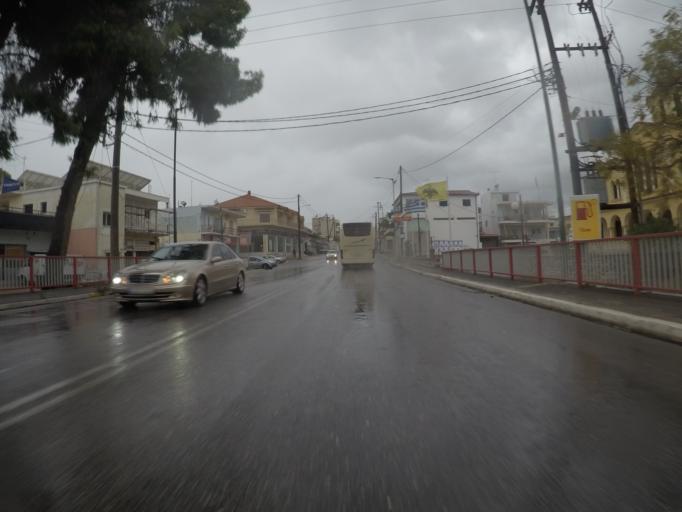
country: GR
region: Peloponnese
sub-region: Nomos Messinias
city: Kalamata
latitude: 37.0413
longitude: 22.0965
